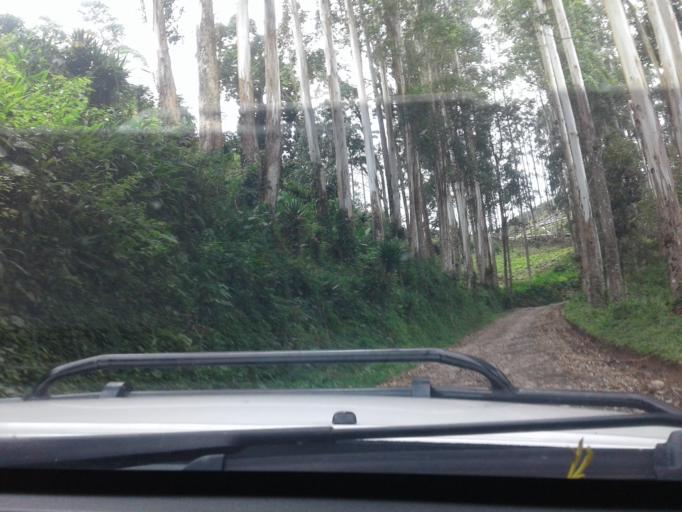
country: NI
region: Matagalpa
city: Matagalpa
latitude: 13.0494
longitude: -85.8775
